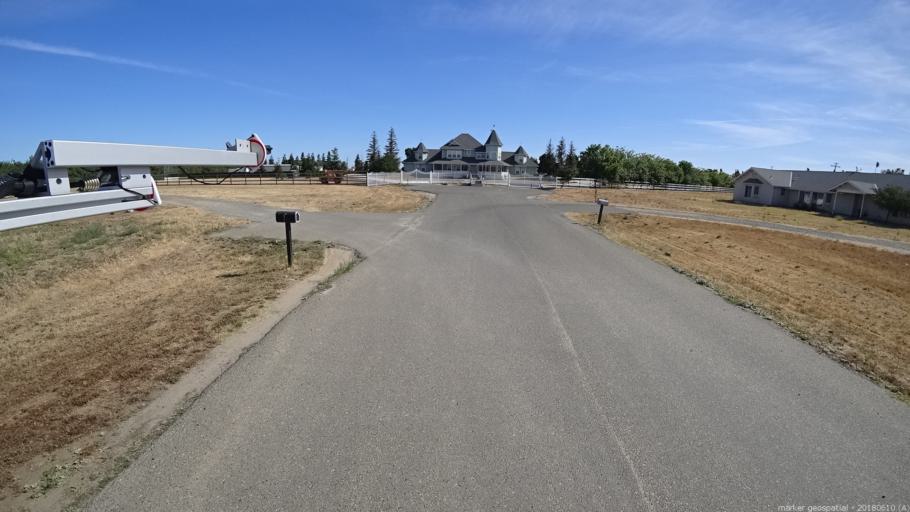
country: US
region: California
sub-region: Madera County
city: Chowchilla
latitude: 37.1032
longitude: -120.2828
